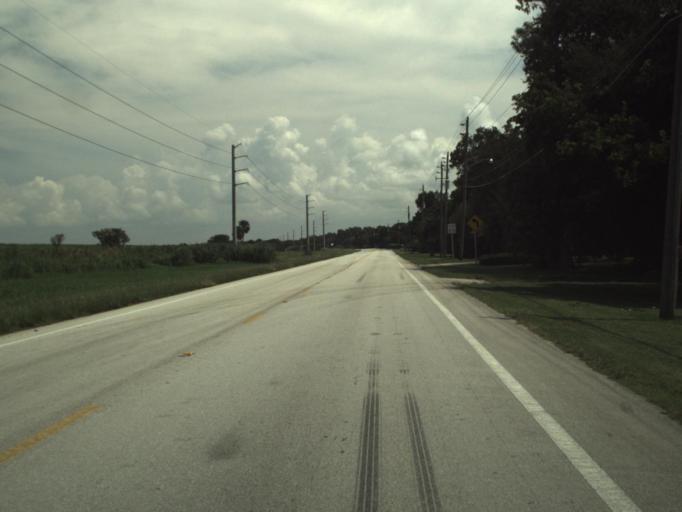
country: US
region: Florida
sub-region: Palm Beach County
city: Pahokee
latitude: 26.8754
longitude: -80.6227
